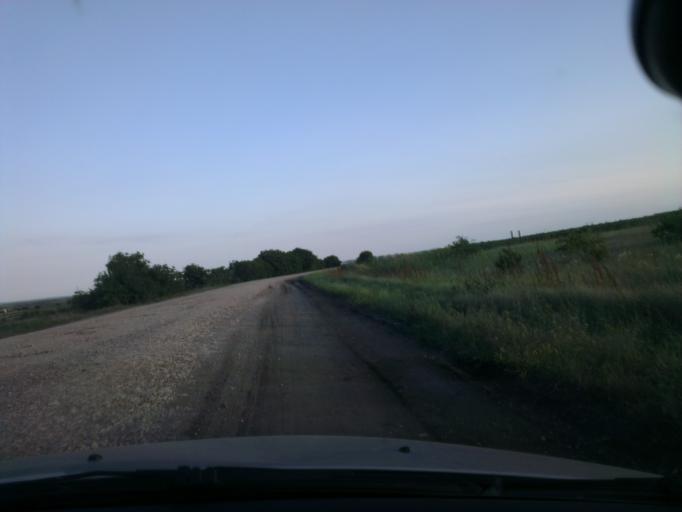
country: MD
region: Cantemir
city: Visniovca
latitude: 46.3428
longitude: 28.4034
